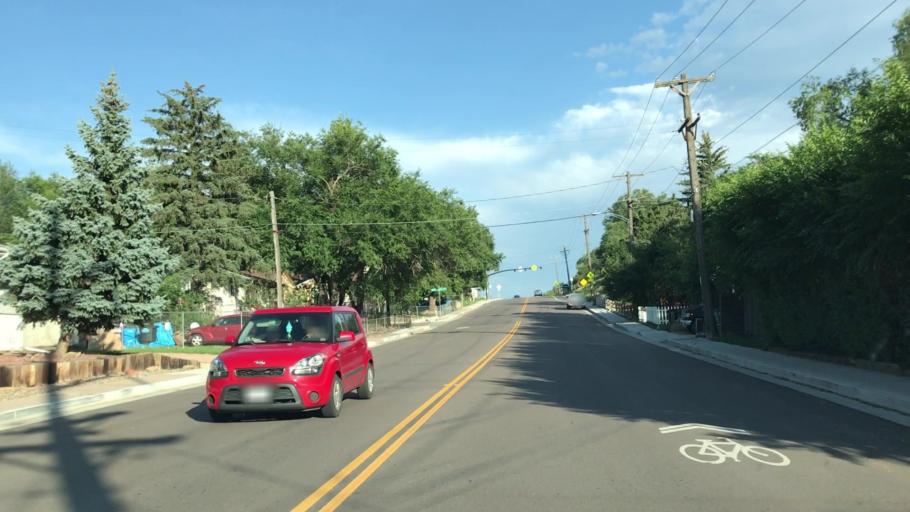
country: US
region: Colorado
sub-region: El Paso County
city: Colorado Springs
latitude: 38.8533
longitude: -104.8637
